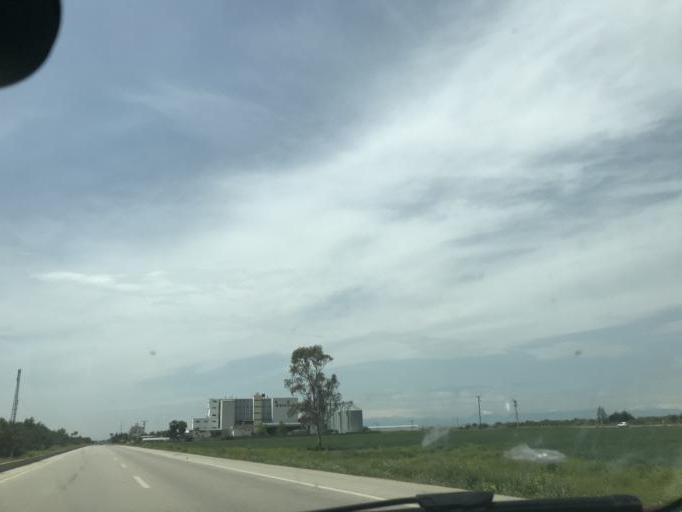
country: TR
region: Adana
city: Yakapinar
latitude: 36.9740
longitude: 35.5003
